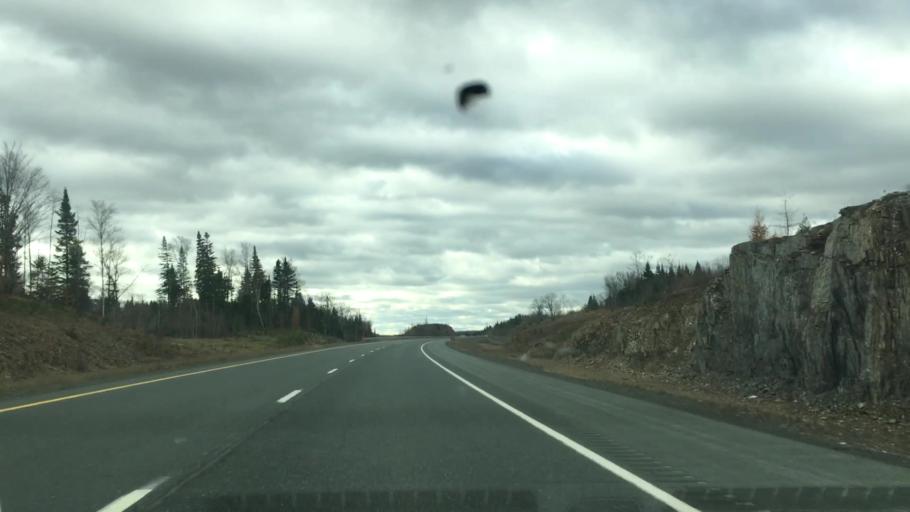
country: US
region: Maine
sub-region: Aroostook County
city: Easton
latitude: 46.6167
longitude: -67.7397
